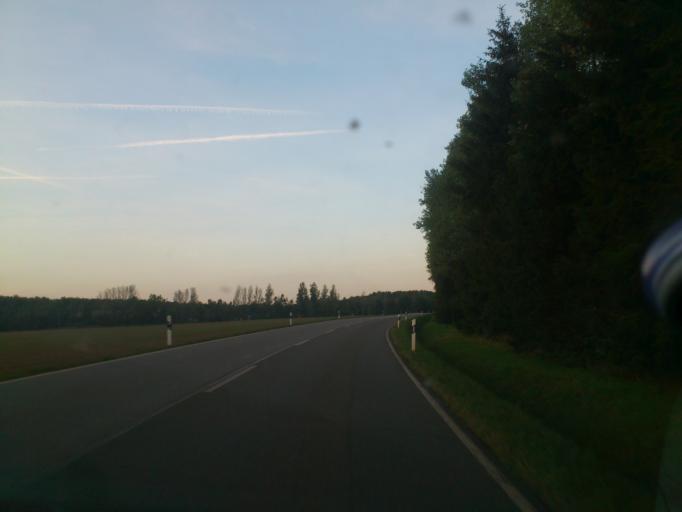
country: DE
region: Saxony
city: Jahnsdorf
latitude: 50.7679
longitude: 12.8400
